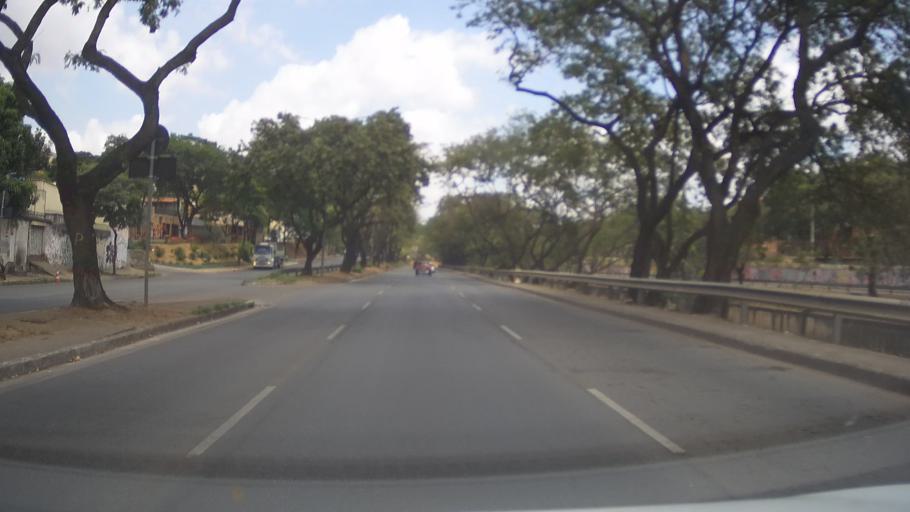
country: BR
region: Minas Gerais
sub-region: Belo Horizonte
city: Belo Horizonte
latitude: -19.9030
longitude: -43.9010
